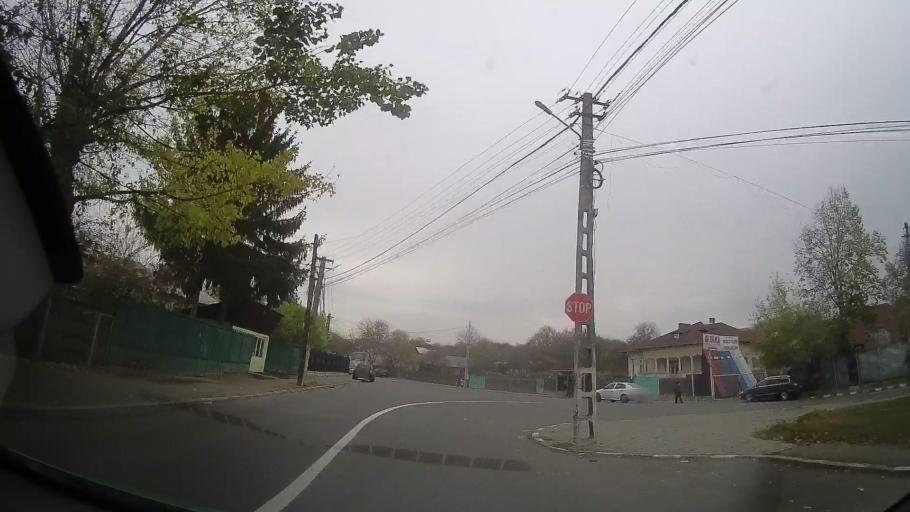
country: RO
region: Prahova
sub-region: Oras Urlati
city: Urlati
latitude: 44.9954
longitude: 26.2305
